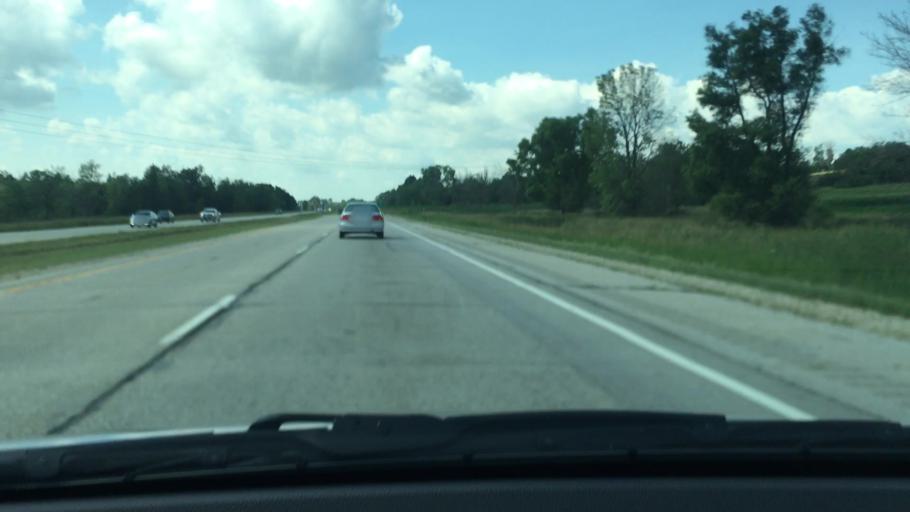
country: US
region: Wisconsin
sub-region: Dodge County
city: Theresa
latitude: 43.4484
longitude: -88.3557
